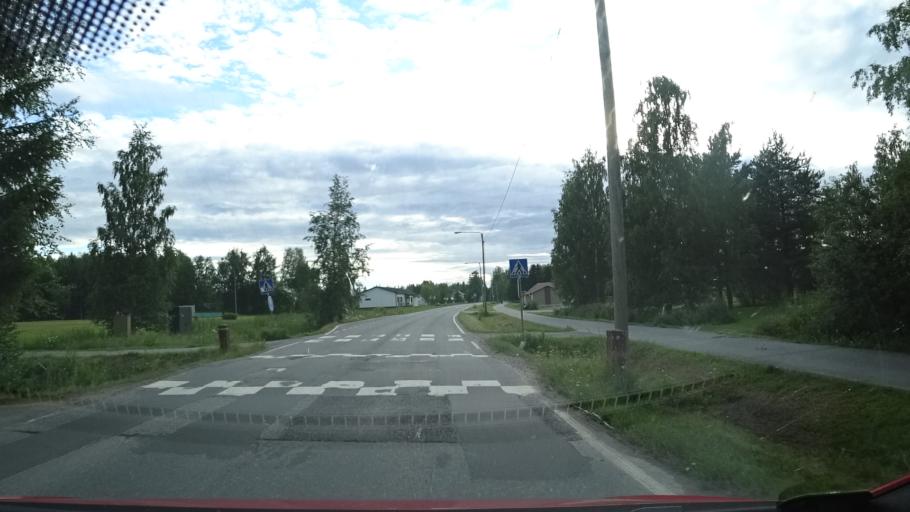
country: FI
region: Northern Ostrobothnia
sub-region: Oulu
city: Liminka
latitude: 64.8079
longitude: 25.4306
